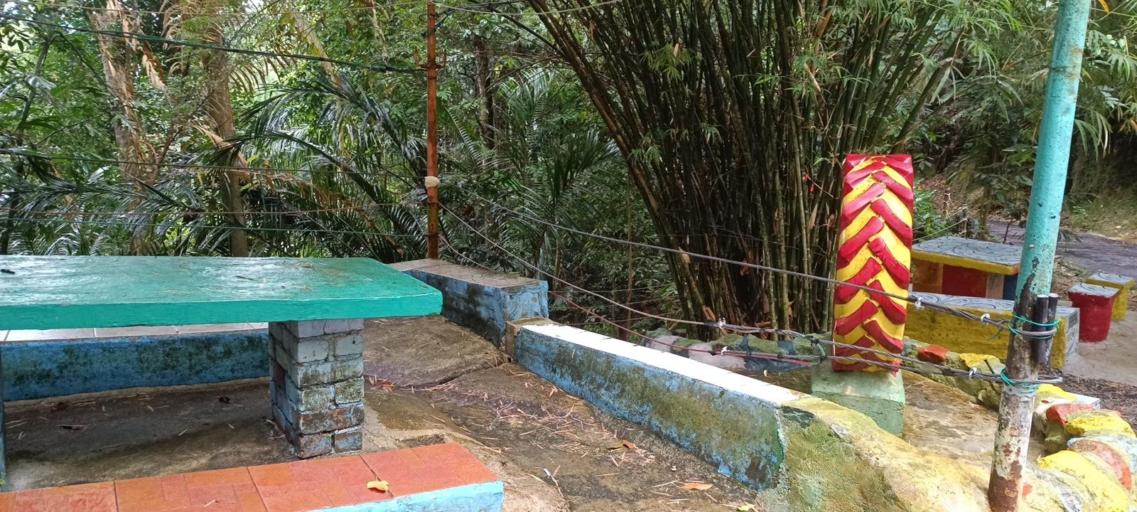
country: MY
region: Perak
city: Taiping
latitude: 4.8646
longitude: 100.7694
